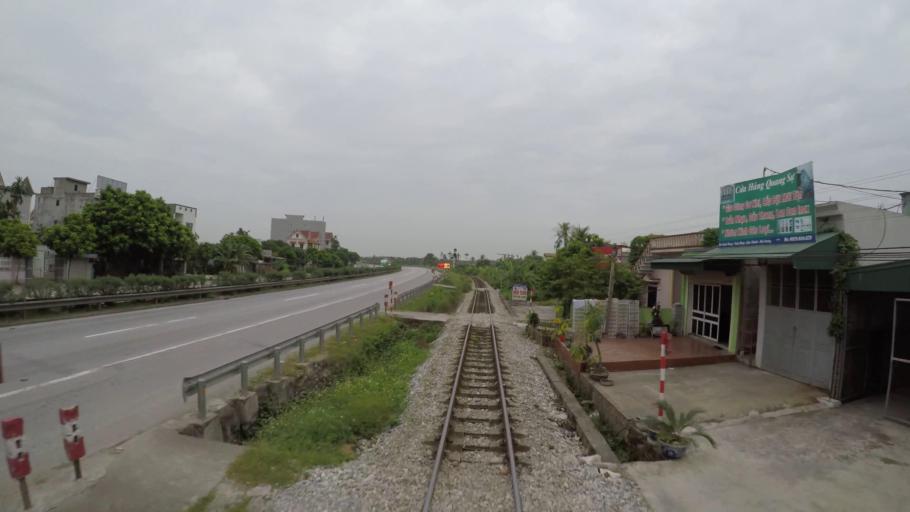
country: VN
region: Hai Duong
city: Phu Thai
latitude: 20.9756
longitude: 106.4338
